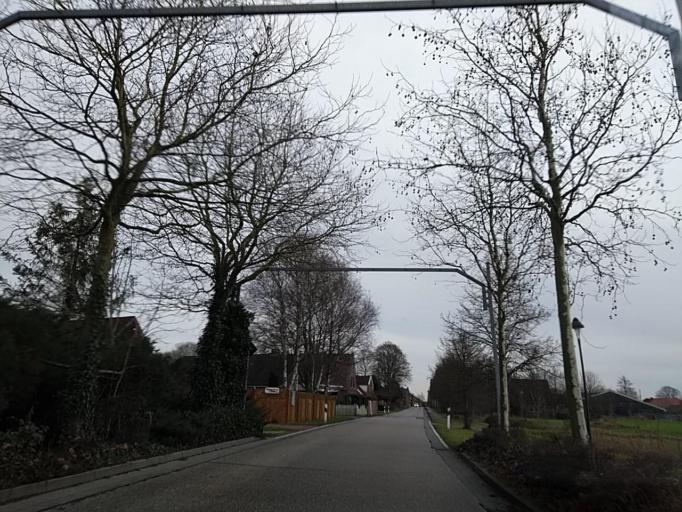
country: DE
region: Lower Saxony
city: Jemgum
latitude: 53.3096
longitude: 7.3117
